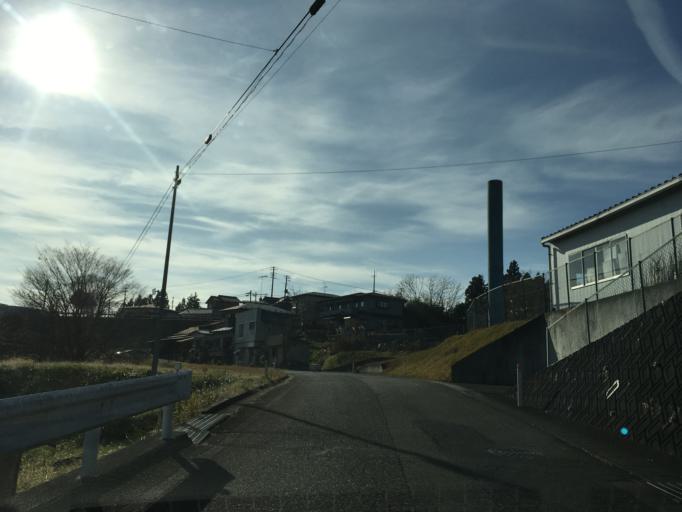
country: JP
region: Iwate
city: Ichinoseki
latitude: 38.7819
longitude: 141.2260
